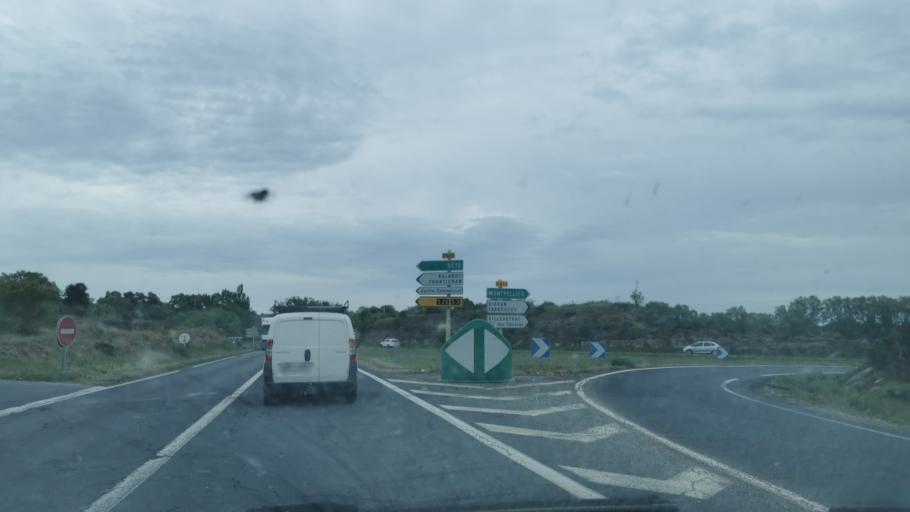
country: FR
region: Languedoc-Roussillon
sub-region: Departement de l'Herault
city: Balaruc-le-Vieux
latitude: 43.4727
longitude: 3.6872
